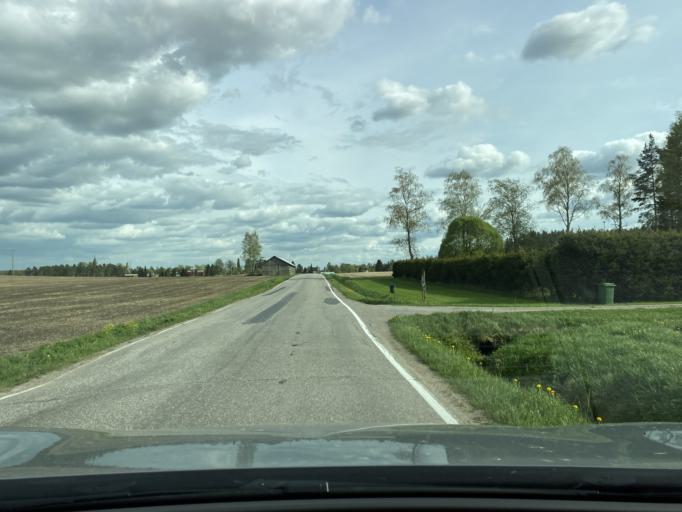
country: FI
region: Varsinais-Suomi
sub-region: Salo
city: Kiikala
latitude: 60.4671
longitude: 23.5428
